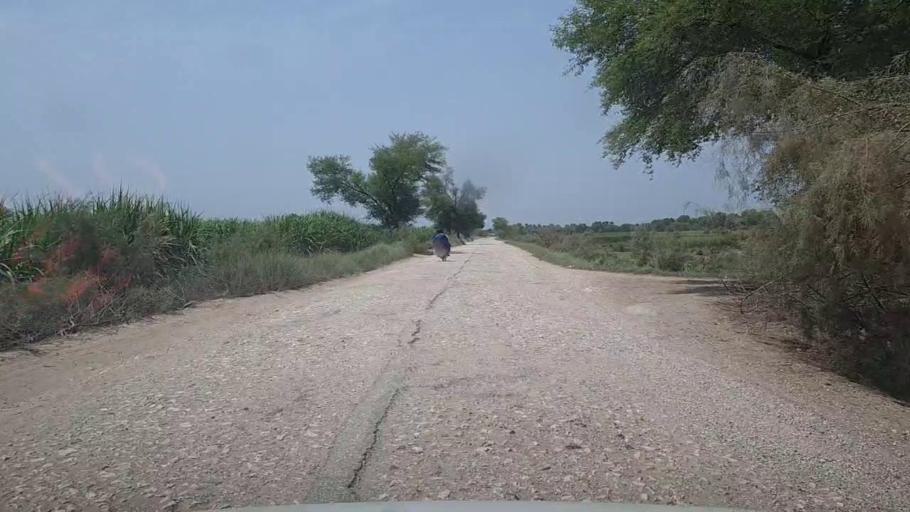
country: PK
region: Sindh
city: Pano Aqil
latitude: 27.8486
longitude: 69.1442
